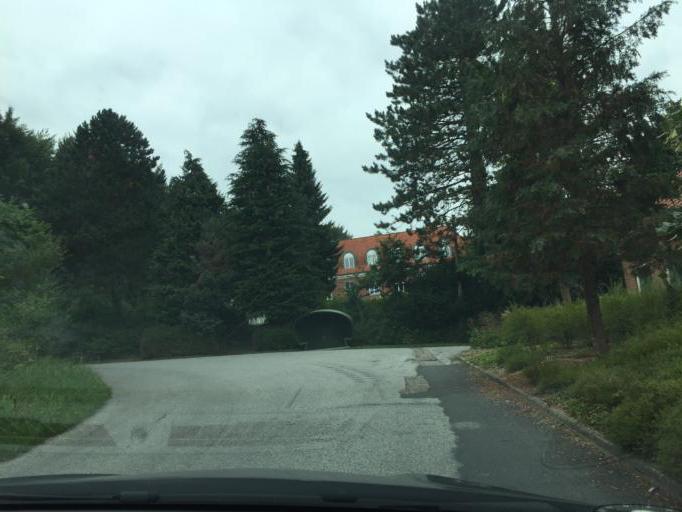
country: DK
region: South Denmark
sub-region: Assens Kommune
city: Arup
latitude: 55.3836
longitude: 10.0474
